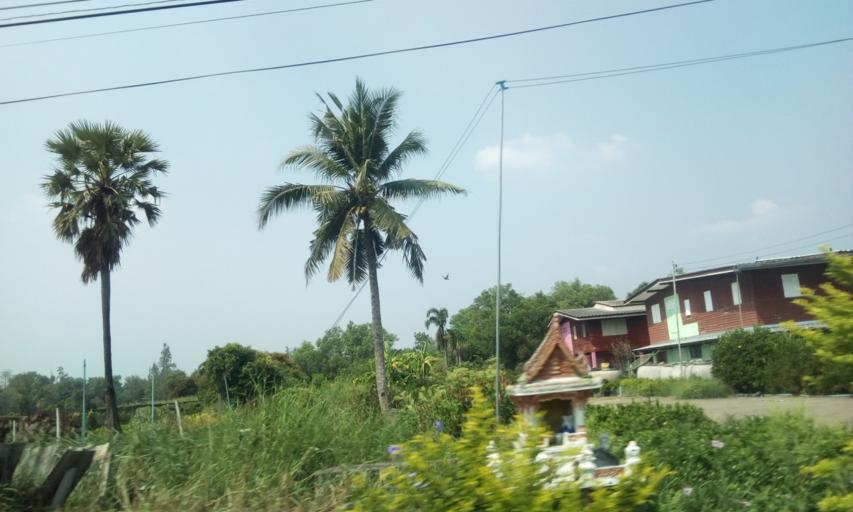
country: TH
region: Nakhon Nayok
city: Ongkharak
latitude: 14.1306
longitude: 100.9525
